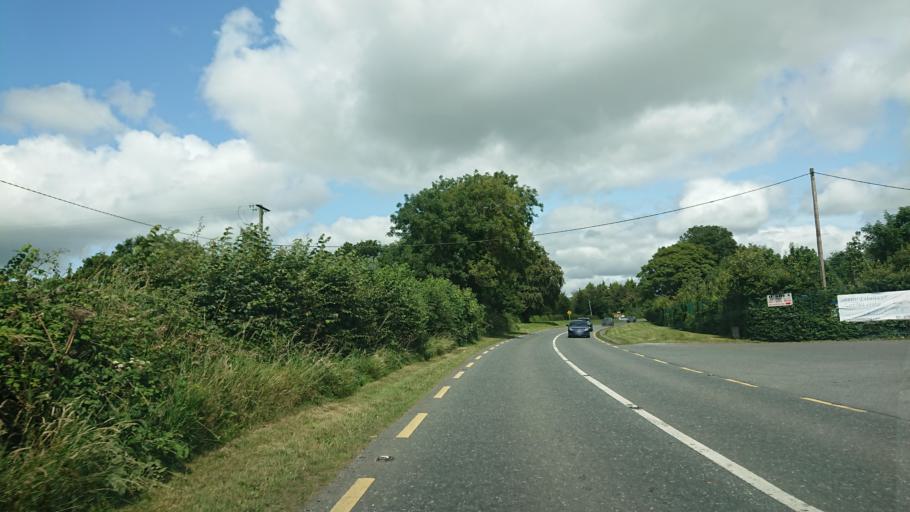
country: IE
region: Leinster
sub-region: Kildare
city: Kilcock
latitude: 53.3824
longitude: -6.7063
